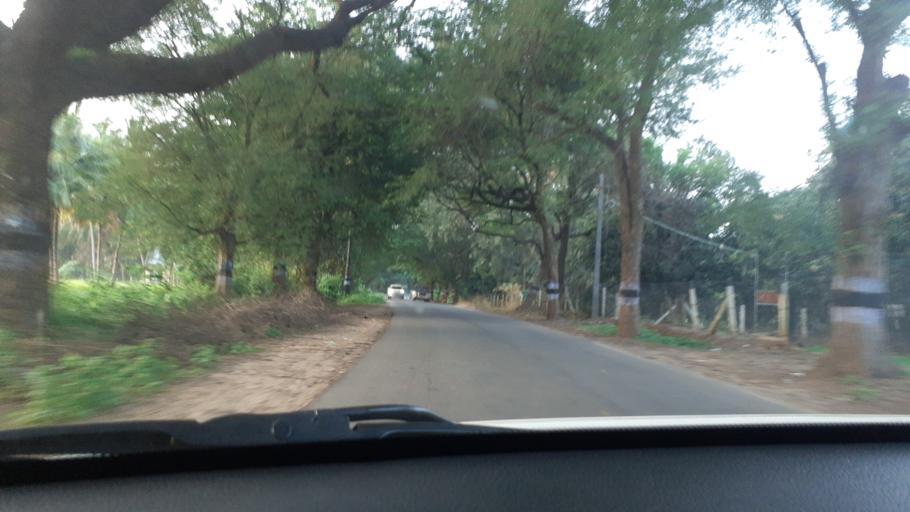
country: IN
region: Tamil Nadu
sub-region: Dindigul
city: Ayakudi
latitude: 10.4037
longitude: 77.5449
